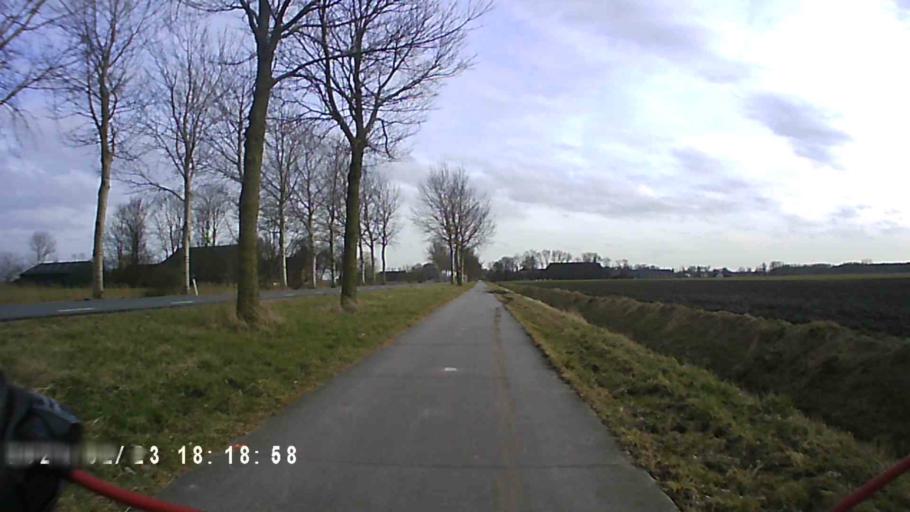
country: NL
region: Groningen
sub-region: Gemeente Bedum
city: Bedum
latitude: 53.3734
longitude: 6.6298
